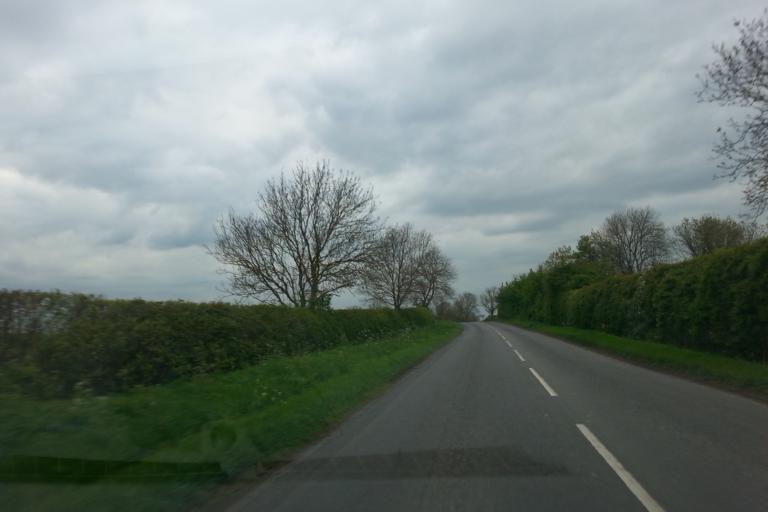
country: GB
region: England
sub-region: Lincolnshire
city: Long Bennington
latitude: 53.0093
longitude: -0.8044
